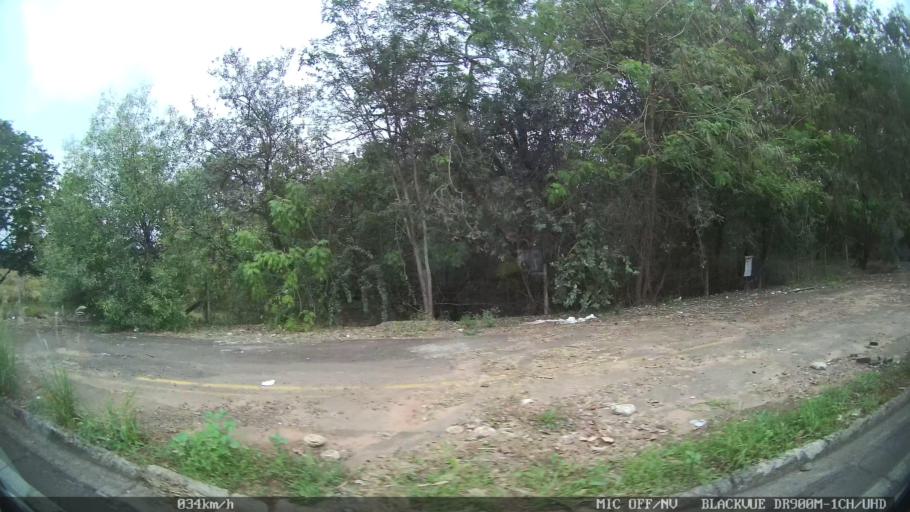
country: BR
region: Sao Paulo
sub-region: Americana
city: Americana
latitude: -22.7052
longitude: -47.3498
